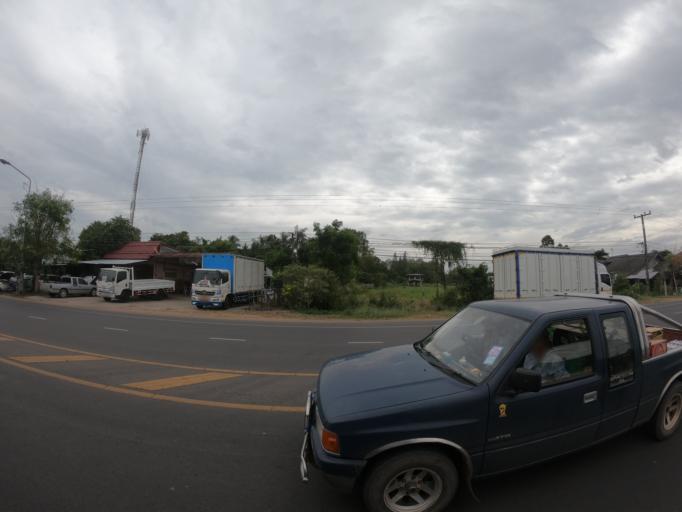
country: TH
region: Roi Et
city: Roi Et
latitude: 16.0794
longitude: 103.6950
